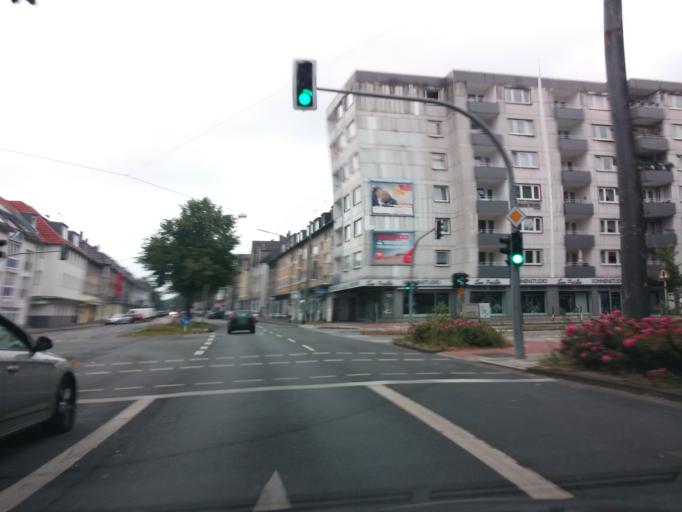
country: DE
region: North Rhine-Westphalia
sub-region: Regierungsbezirk Munster
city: Gladbeck
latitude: 51.5912
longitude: 7.0515
